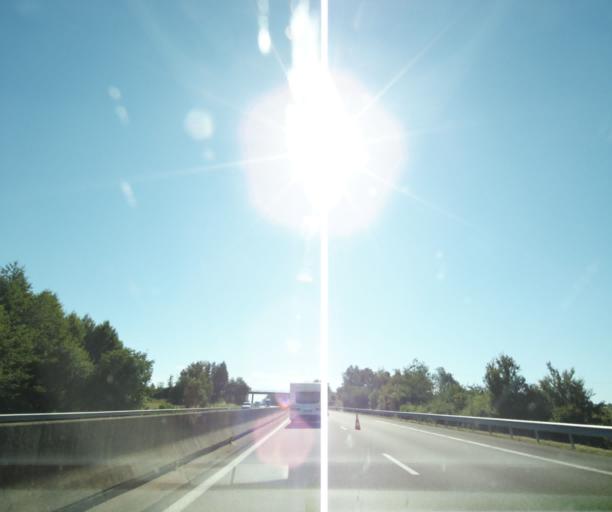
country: FR
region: Champagne-Ardenne
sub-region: Departement de la Haute-Marne
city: Rolampont
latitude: 47.9477
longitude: 5.3338
